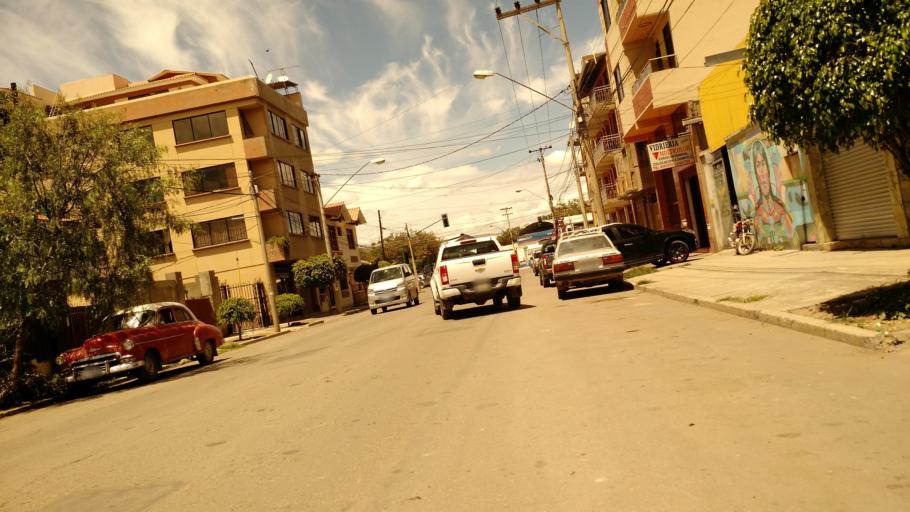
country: BO
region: Cochabamba
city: Cochabamba
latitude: -17.3970
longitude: -66.1658
